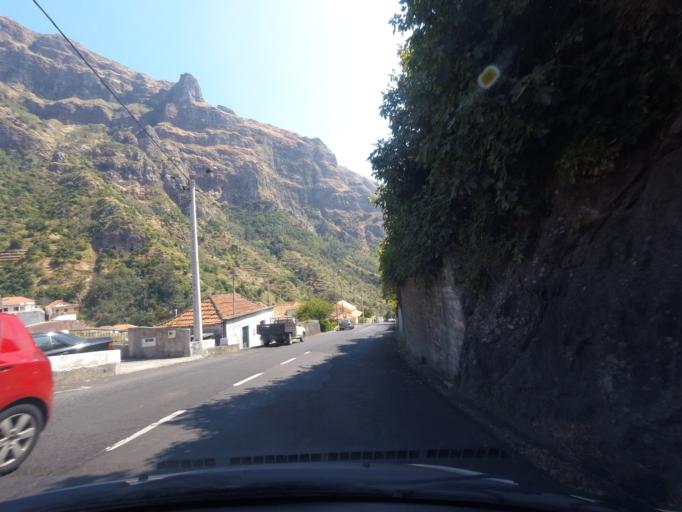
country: PT
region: Madeira
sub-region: Camara de Lobos
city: Curral das Freiras
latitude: 32.7284
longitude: -17.0287
